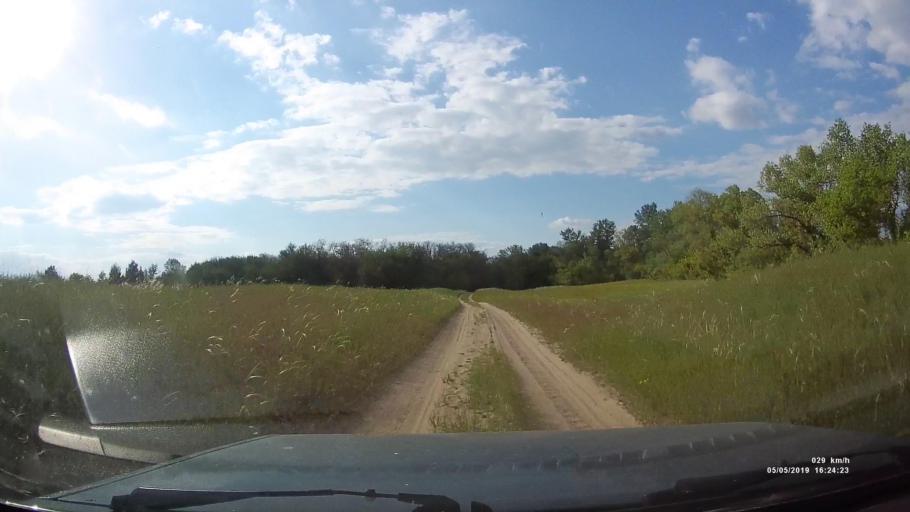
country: RU
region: Rostov
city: Konstantinovsk
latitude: 47.7592
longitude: 41.0264
